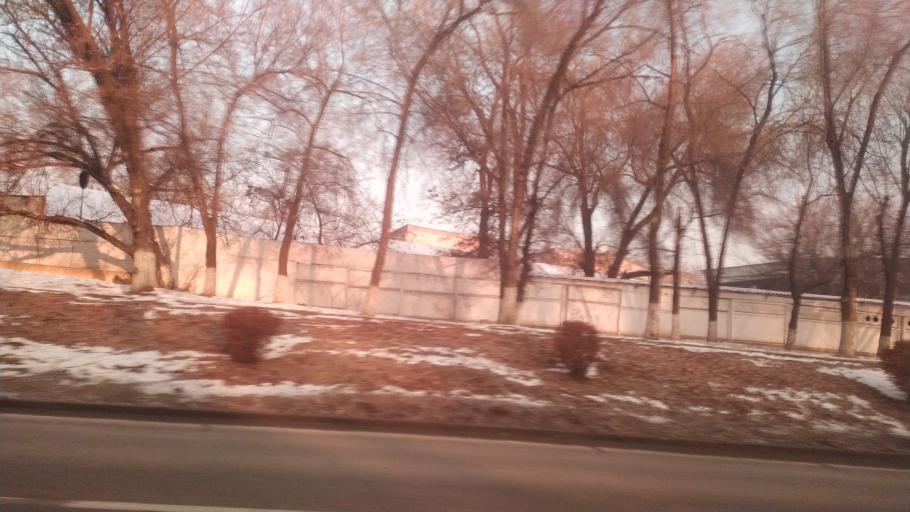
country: KZ
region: Almaty Qalasy
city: Almaty
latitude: 43.2659
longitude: 76.9096
